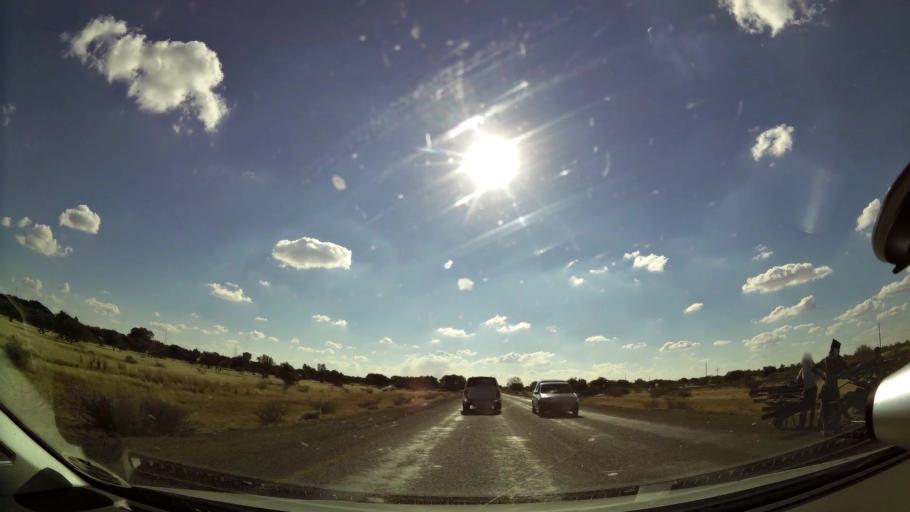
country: ZA
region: Northern Cape
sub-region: Frances Baard District Municipality
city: Kimberley
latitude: -28.7935
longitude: 24.7871
